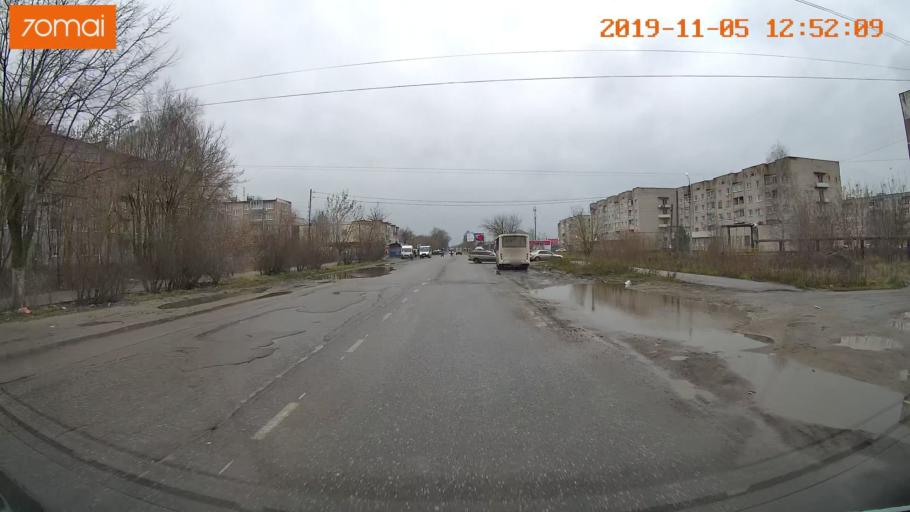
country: RU
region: Ivanovo
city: Kokhma
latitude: 56.9409
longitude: 41.1094
